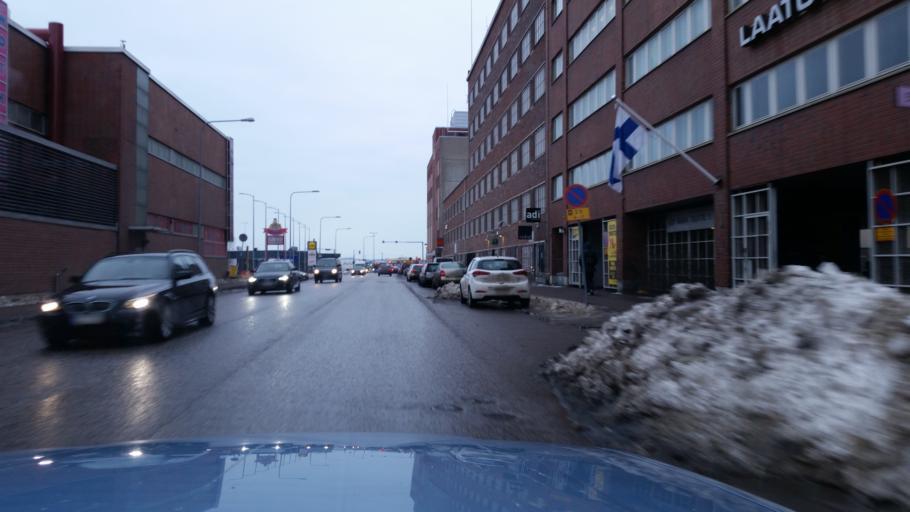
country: FI
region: Uusimaa
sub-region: Helsinki
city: Helsinki
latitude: 60.1909
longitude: 24.9762
